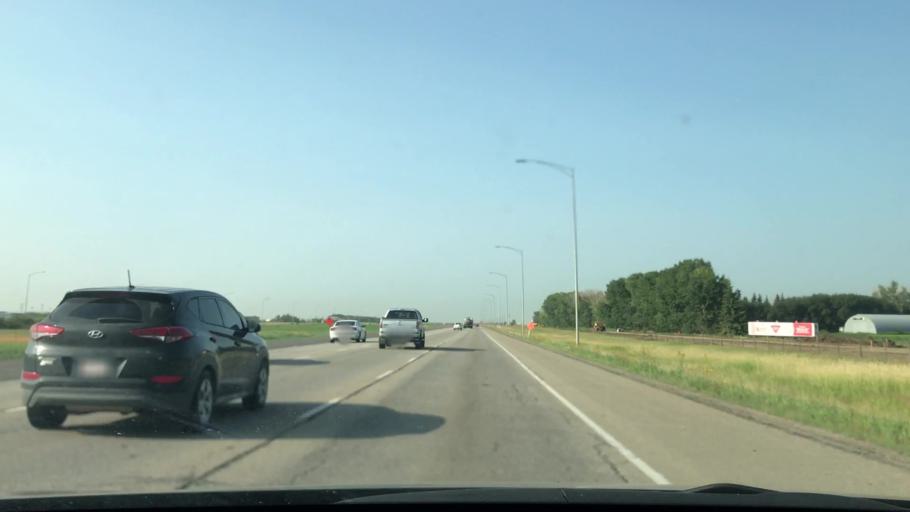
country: CA
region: Alberta
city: Leduc
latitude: 53.3664
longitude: -113.5336
